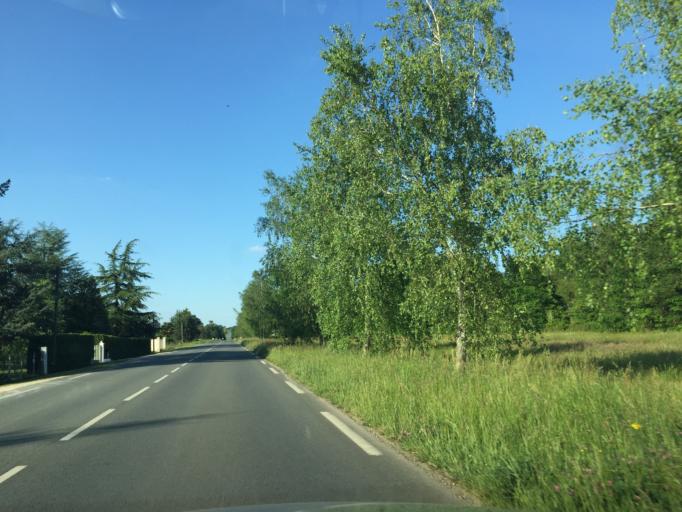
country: FR
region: Aquitaine
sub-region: Departement de la Dordogne
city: La Roche-Chalais
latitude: 45.1722
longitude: 0.0168
